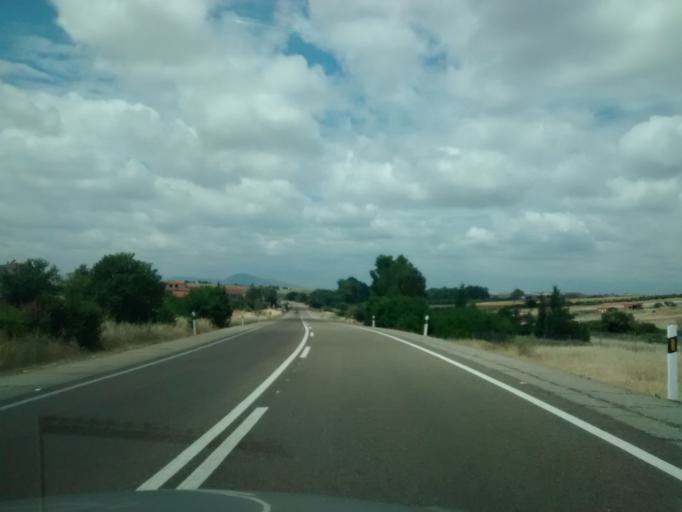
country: ES
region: Extremadura
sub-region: Provincia de Badajoz
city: Trujillanos
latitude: 38.9396
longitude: -6.2982
